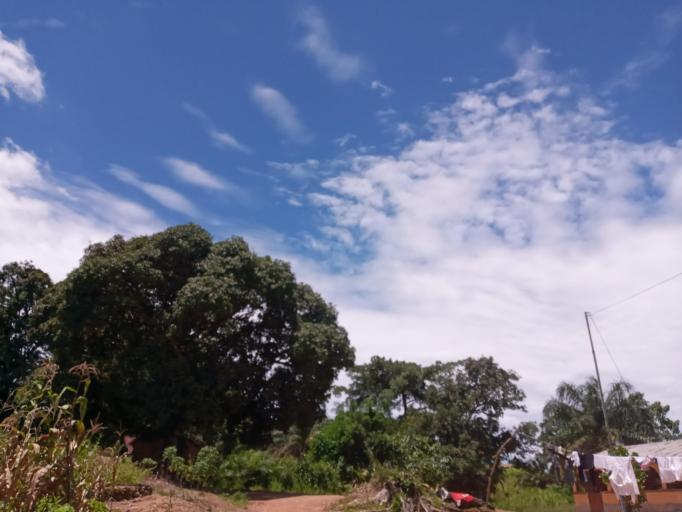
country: SL
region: Eastern Province
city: Koidu
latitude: 8.6528
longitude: -10.9619
